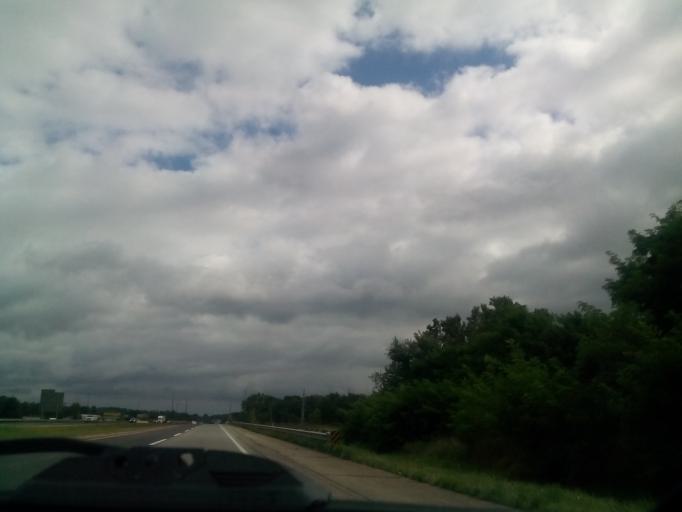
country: US
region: Indiana
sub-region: Steuben County
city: Fremont
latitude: 41.7324
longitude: -84.9731
